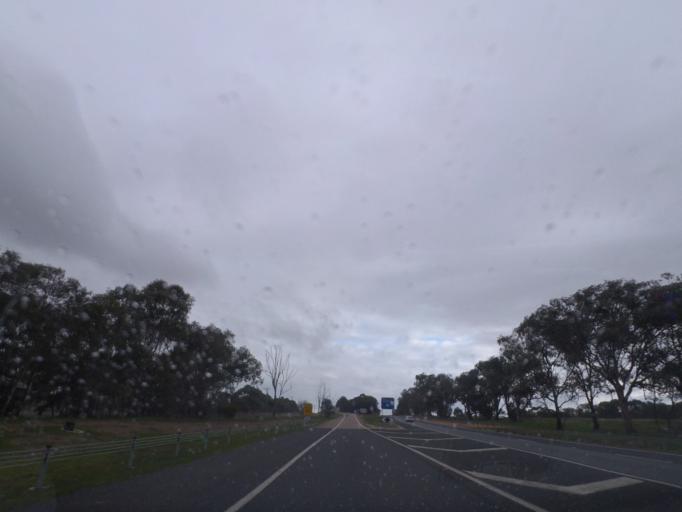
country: AU
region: Victoria
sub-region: Wangaratta
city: Wangaratta
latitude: -36.2183
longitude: 146.4480
